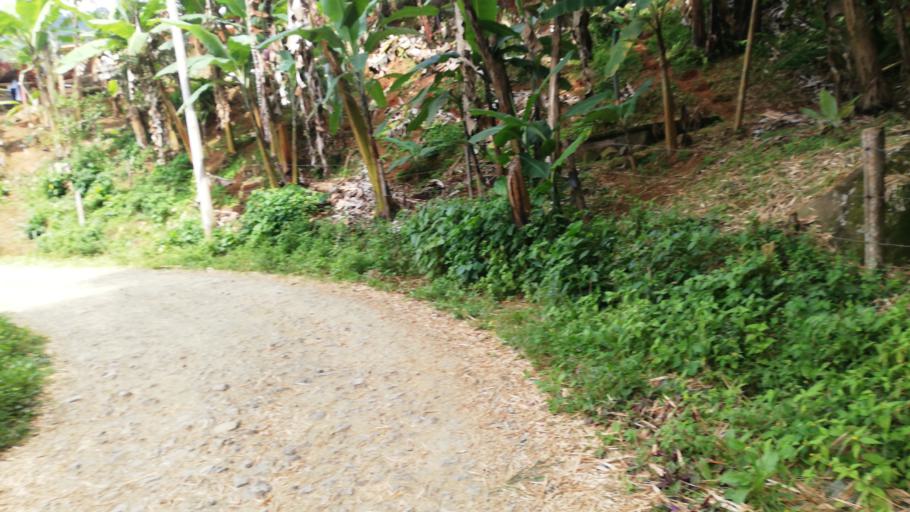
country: CO
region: Valle del Cauca
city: Yumbo
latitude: 3.6279
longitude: -76.5448
